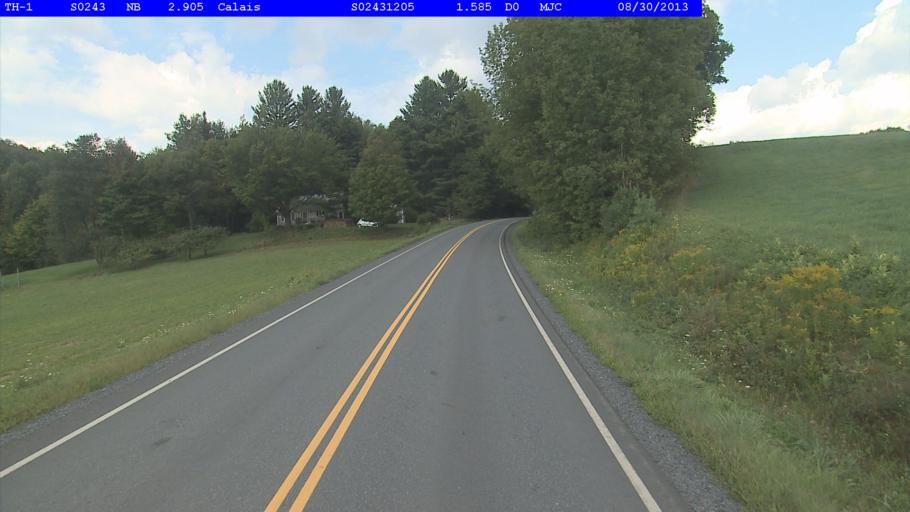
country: US
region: Vermont
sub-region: Washington County
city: Montpelier
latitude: 44.3558
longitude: -72.5108
